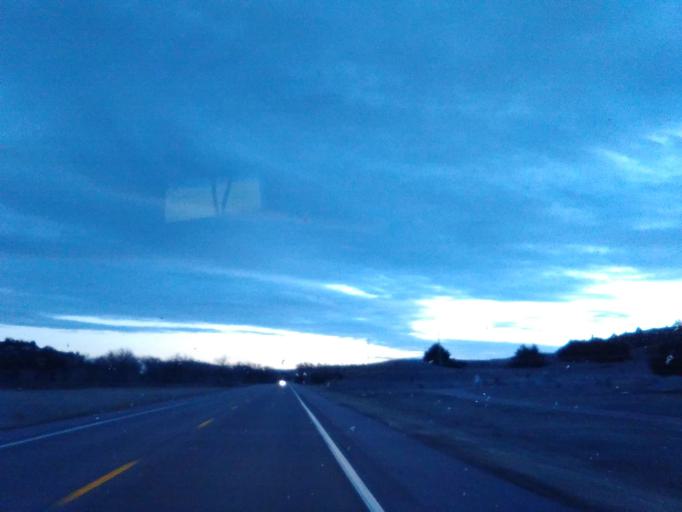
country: US
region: Nebraska
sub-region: Garden County
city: Oshkosh
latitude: 41.3078
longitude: -102.1251
